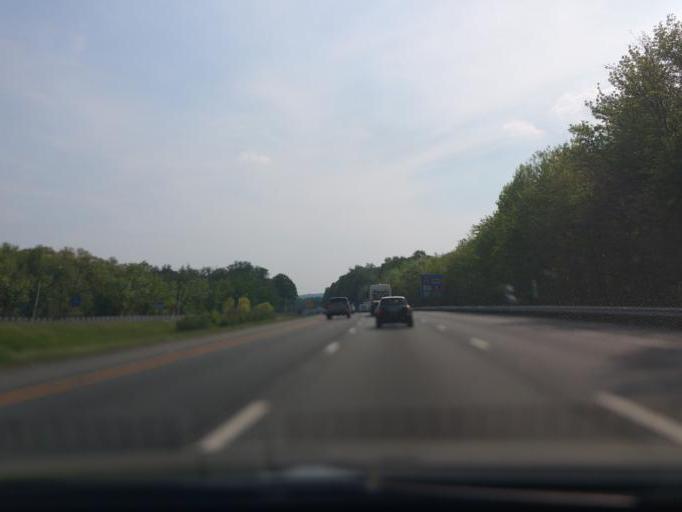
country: US
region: Maryland
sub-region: Harford County
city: Riverside
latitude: 39.4973
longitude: -76.2343
